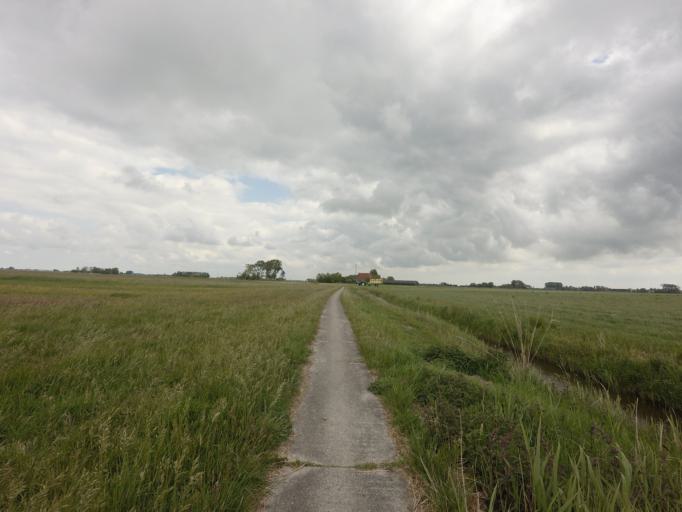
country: NL
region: Friesland
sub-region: Gemeente Littenseradiel
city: Wommels
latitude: 53.1090
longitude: 5.6076
